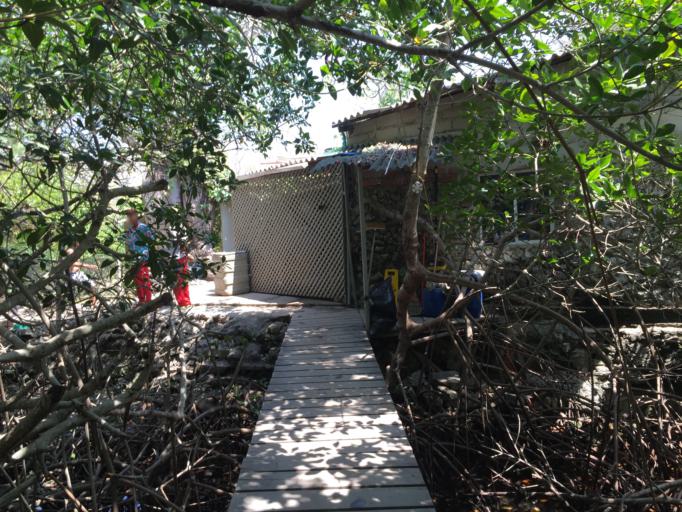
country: CO
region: Bolivar
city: Turbana
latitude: 10.1770
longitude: -75.7553
